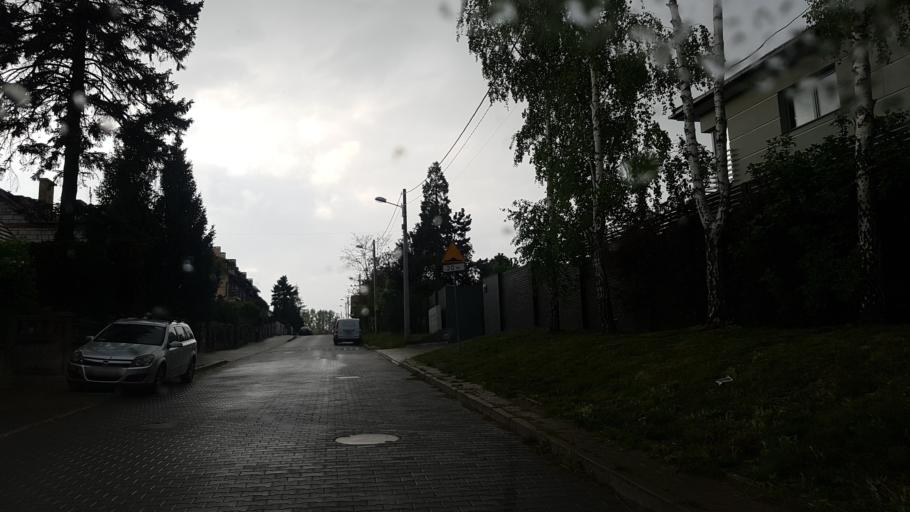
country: PL
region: West Pomeranian Voivodeship
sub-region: Szczecin
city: Szczecin
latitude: 53.4654
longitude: 14.5467
